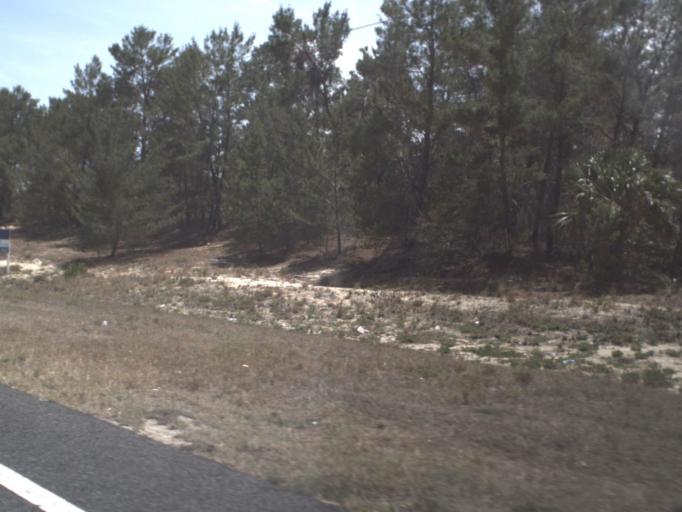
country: US
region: Florida
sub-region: Brevard County
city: Port Saint John
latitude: 28.5345
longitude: -80.8243
